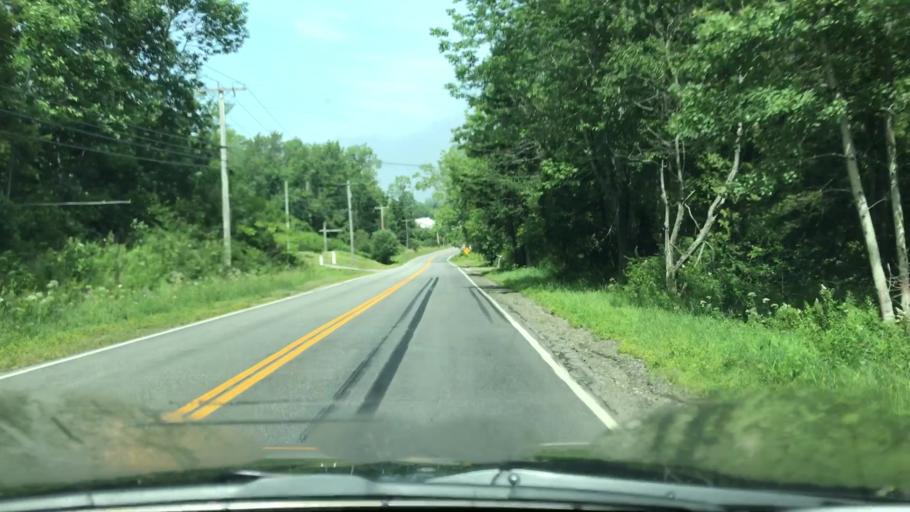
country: US
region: Maine
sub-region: Waldo County
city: Lincolnville
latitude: 44.2693
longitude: -69.0161
